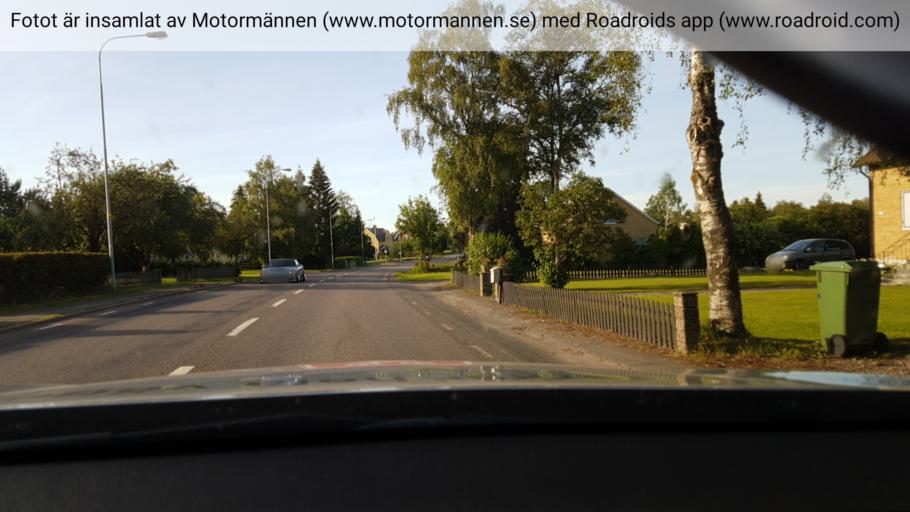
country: SE
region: Vaestra Goetaland
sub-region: Falkopings Kommun
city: Falkoeping
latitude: 58.0819
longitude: 13.5160
